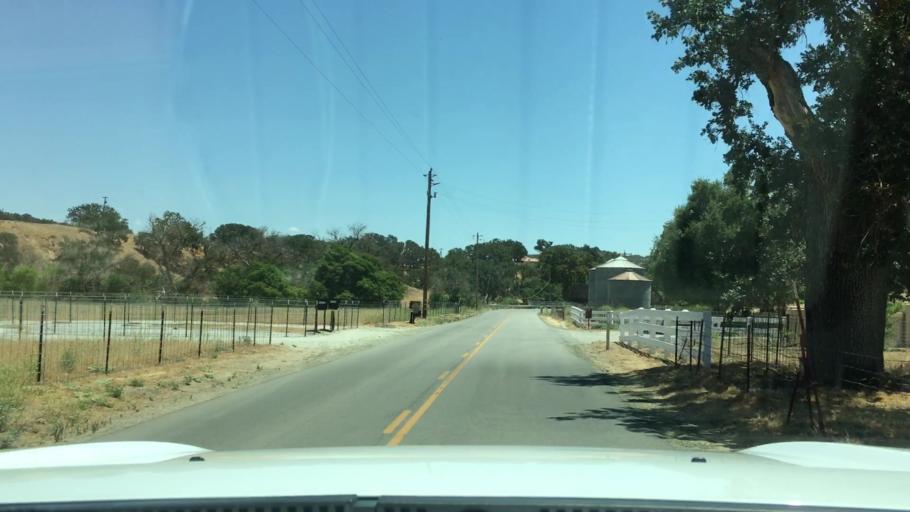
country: US
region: California
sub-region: San Luis Obispo County
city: Paso Robles
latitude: 35.6024
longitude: -120.6044
